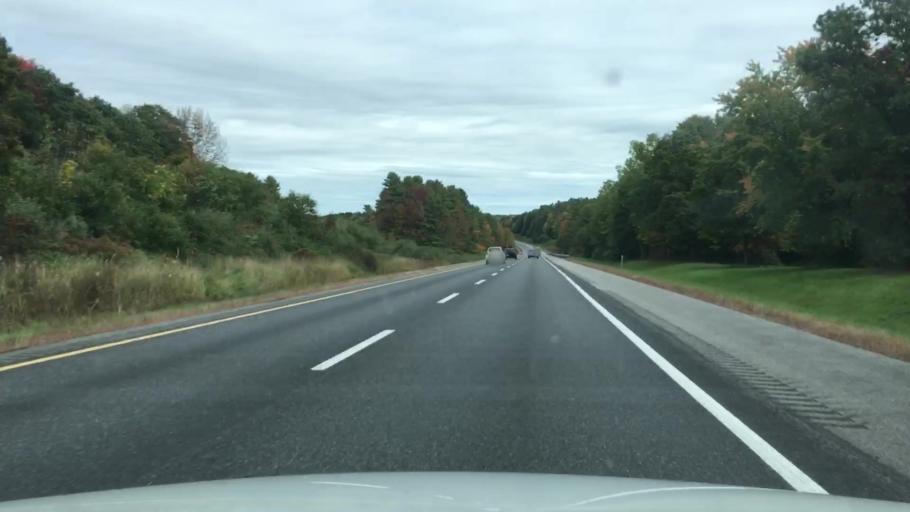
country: US
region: Maine
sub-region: Sagadahoc County
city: Richmond
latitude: 44.0401
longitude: -69.8997
